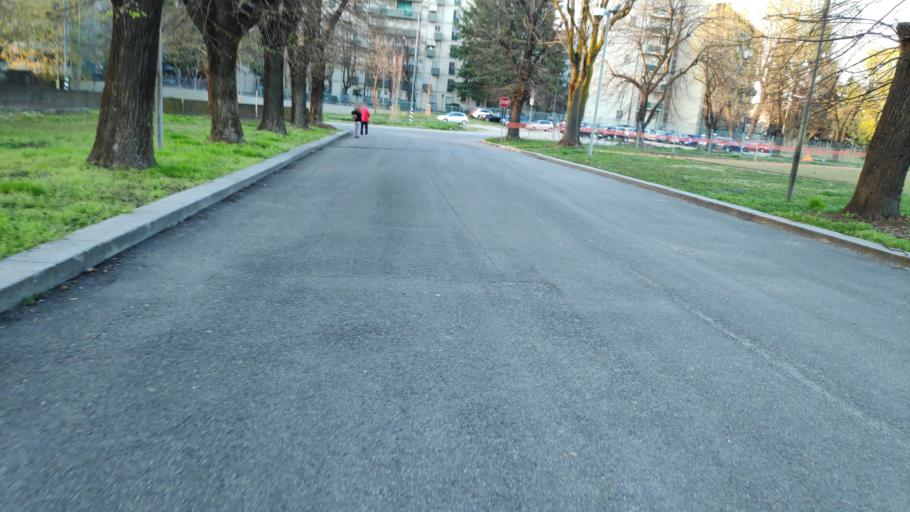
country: IT
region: Lombardy
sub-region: Citta metropolitana di Milano
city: Linate
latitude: 45.4442
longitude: 9.2532
